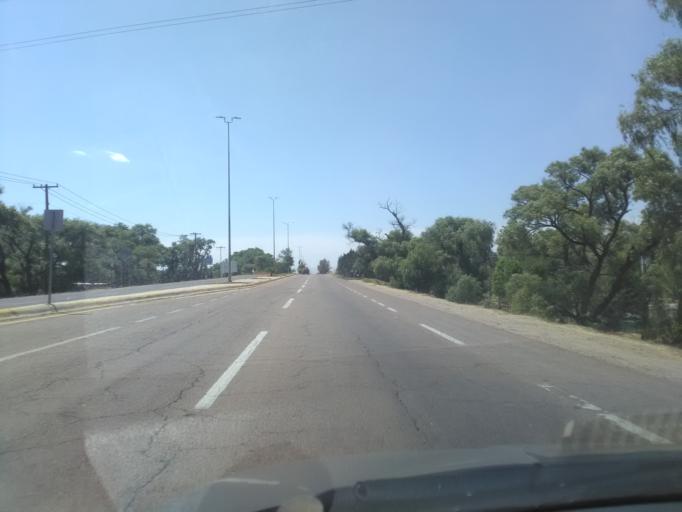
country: MX
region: Durango
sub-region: Durango
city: Jose Refugio Salcido
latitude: 24.0252
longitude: -104.5626
